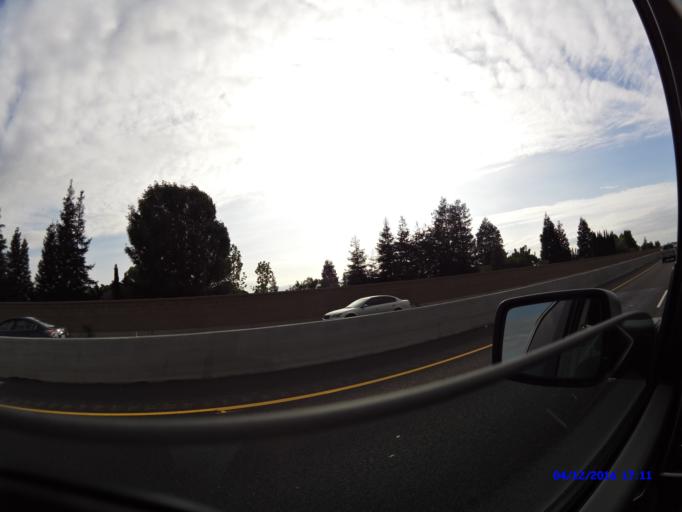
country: US
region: California
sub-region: San Joaquin County
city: Manteca
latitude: 37.8163
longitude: -121.2099
